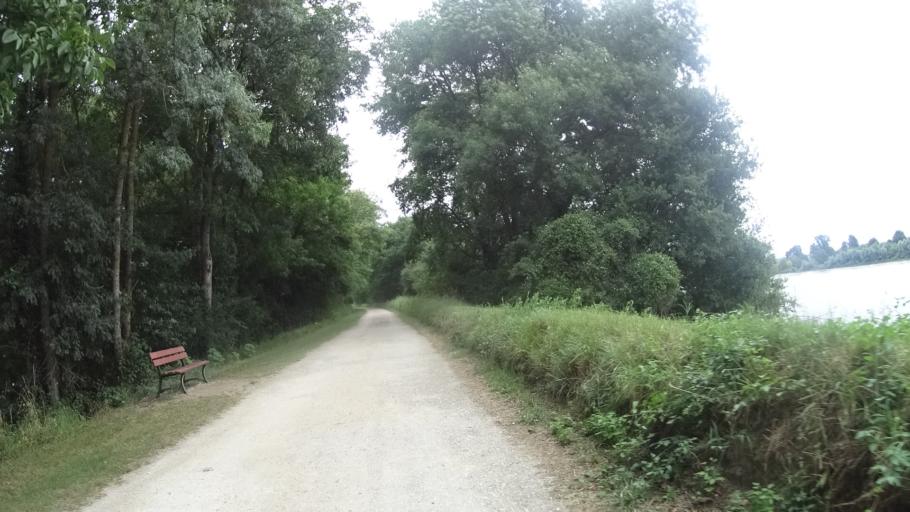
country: FR
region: Centre
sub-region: Departement du Loir-et-Cher
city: La Chaussee-Saint-Victor
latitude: 47.6222
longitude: 1.3906
